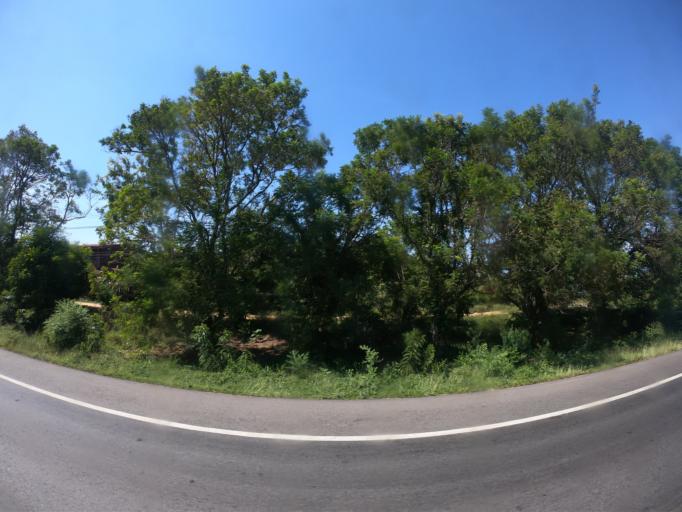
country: TH
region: Khon Kaen
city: Non Sila
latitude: 15.9992
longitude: 102.7014
